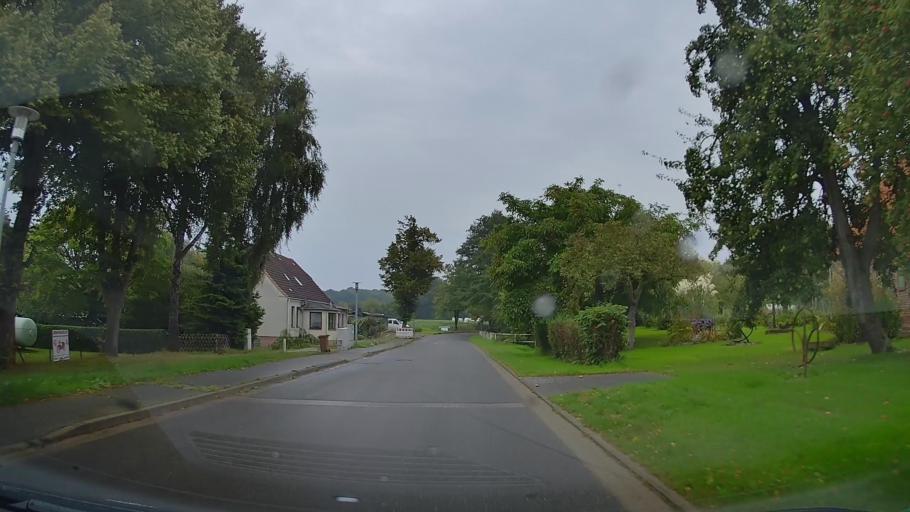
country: DE
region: Mecklenburg-Vorpommern
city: Kalkhorst
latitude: 54.0001
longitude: 11.0875
